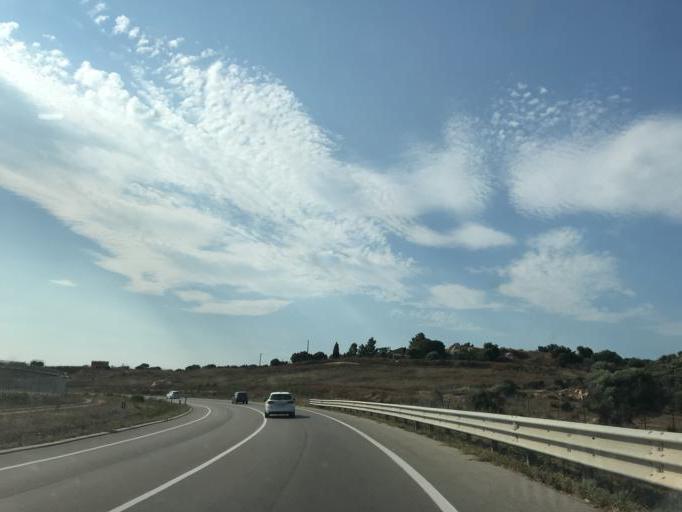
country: IT
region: Sardinia
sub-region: Provincia di Olbia-Tempio
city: Olbia
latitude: 40.9081
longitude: 9.5363
